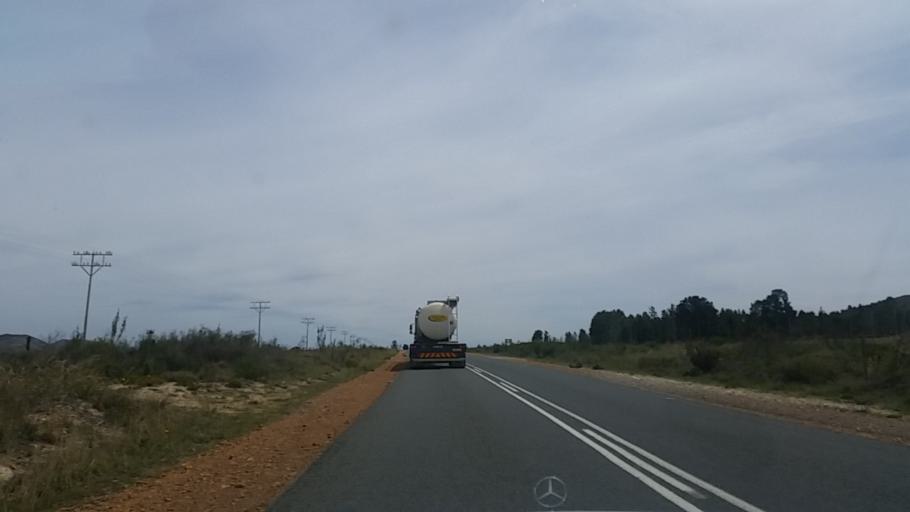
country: ZA
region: Western Cape
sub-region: Eden District Municipality
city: Knysna
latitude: -33.7610
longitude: 22.8777
